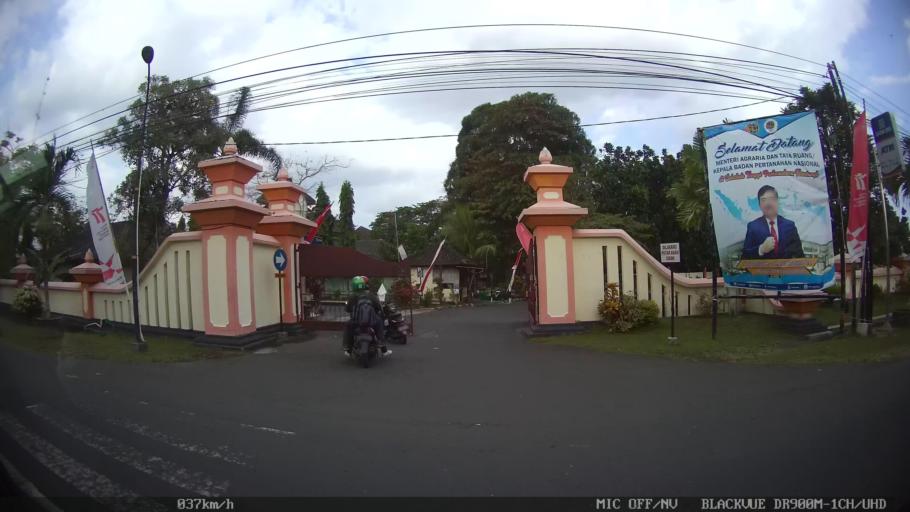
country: ID
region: Daerah Istimewa Yogyakarta
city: Yogyakarta
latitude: -7.7826
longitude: 110.3424
